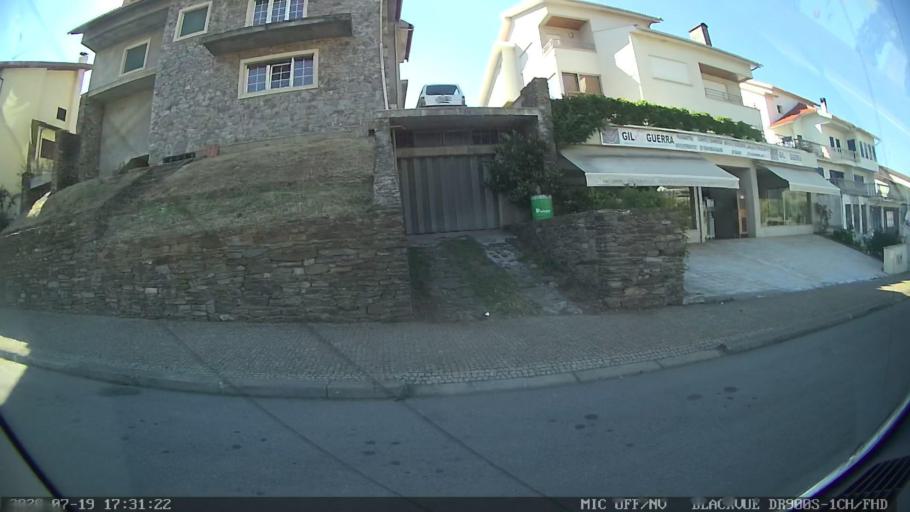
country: PT
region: Braganca
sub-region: Braganca Municipality
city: Braganca
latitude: 41.7888
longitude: -6.7722
